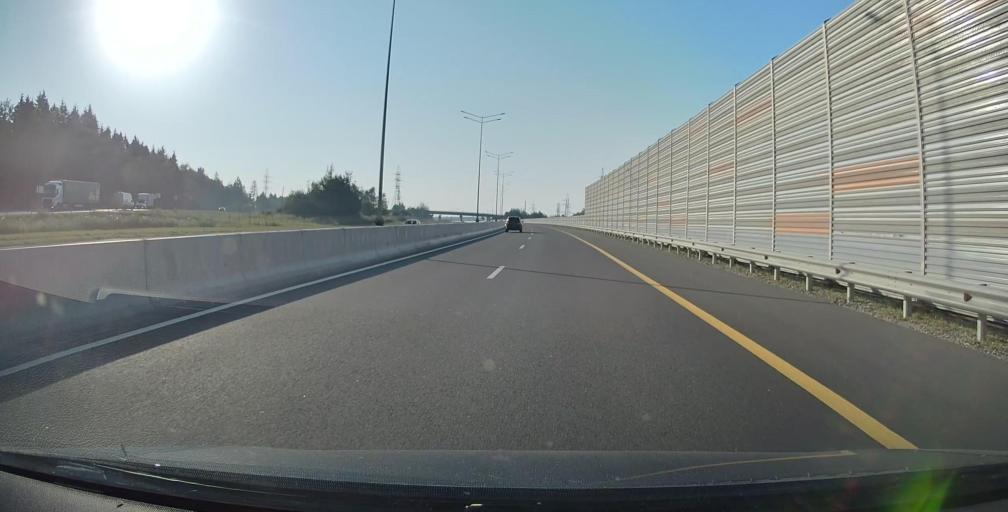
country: RU
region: Moskovskaya
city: Podosinki
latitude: 56.1859
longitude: 37.6010
